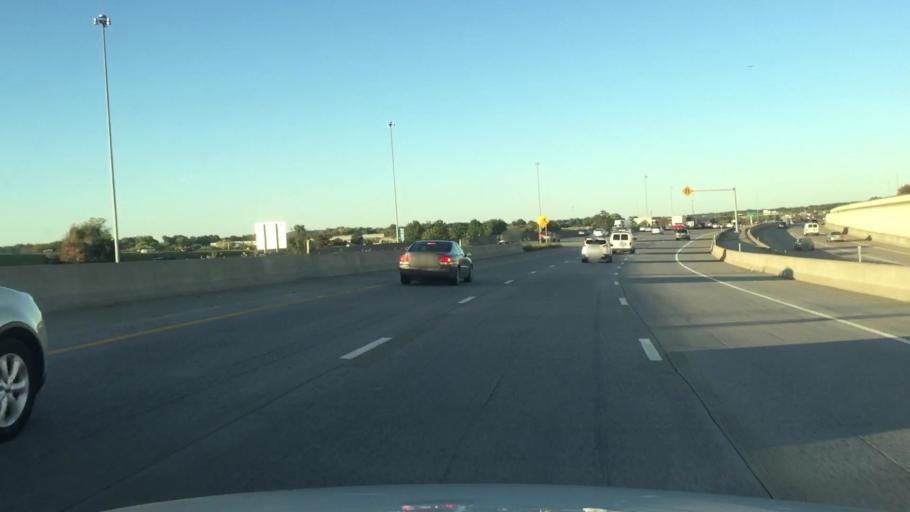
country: US
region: Kansas
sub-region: Johnson County
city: Lenexa
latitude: 38.9765
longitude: -94.7130
